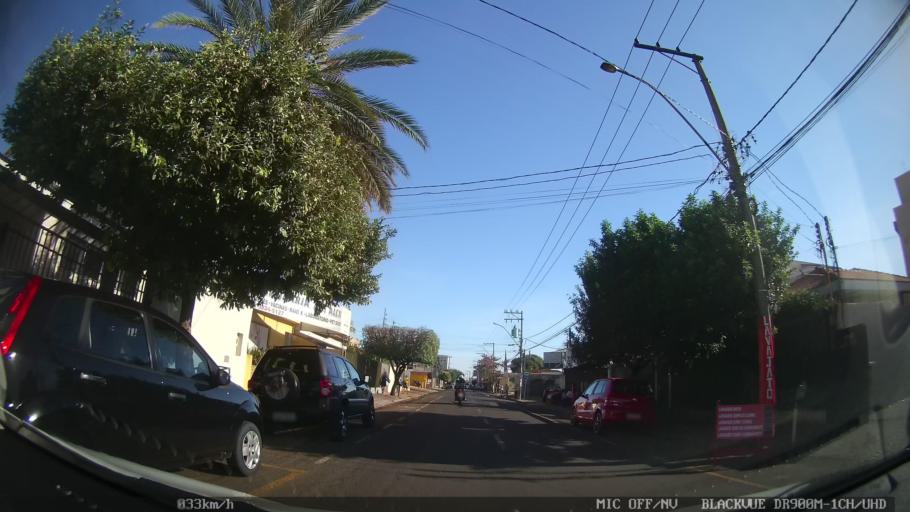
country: BR
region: Sao Paulo
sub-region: Sao Jose Do Rio Preto
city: Sao Jose do Rio Preto
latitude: -20.7995
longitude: -49.3696
